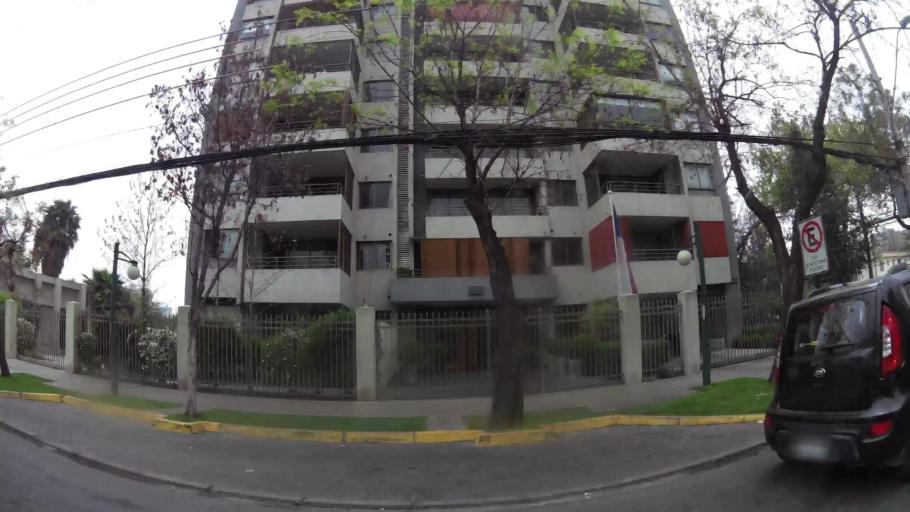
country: CL
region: Santiago Metropolitan
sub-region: Provincia de Santiago
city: Villa Presidente Frei, Nunoa, Santiago, Chile
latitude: -33.4577
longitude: -70.6030
